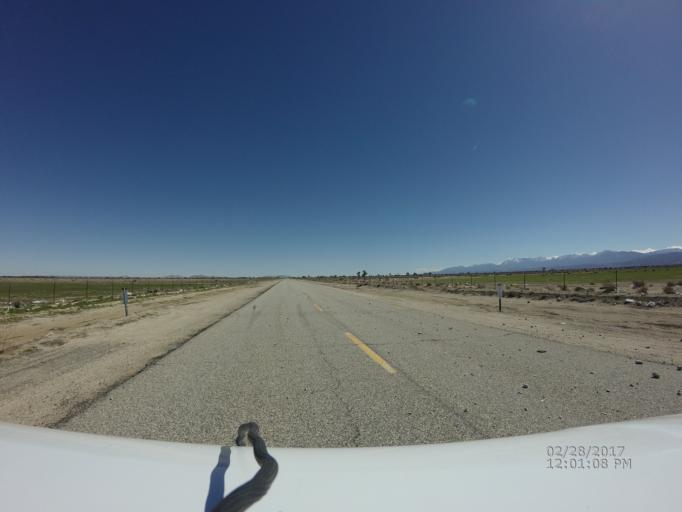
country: US
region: California
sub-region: Los Angeles County
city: Palmdale
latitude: 34.5948
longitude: -118.0540
